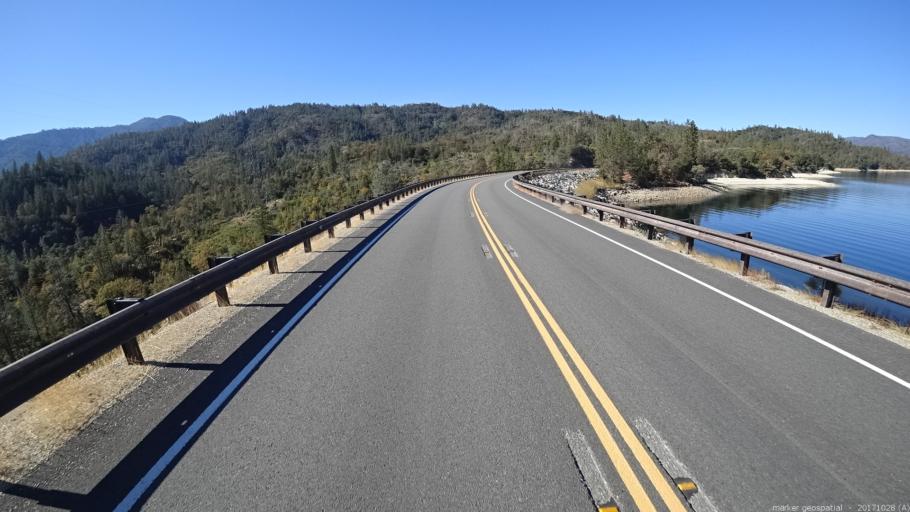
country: US
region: California
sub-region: Shasta County
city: Shasta
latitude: 40.5979
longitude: -122.5453
